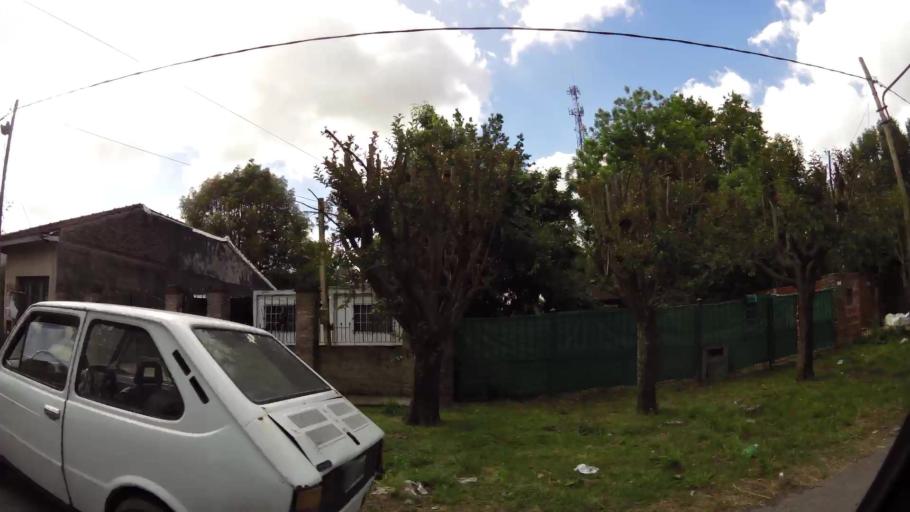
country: AR
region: Buenos Aires
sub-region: Partido de Quilmes
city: Quilmes
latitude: -34.8355
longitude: -58.1881
